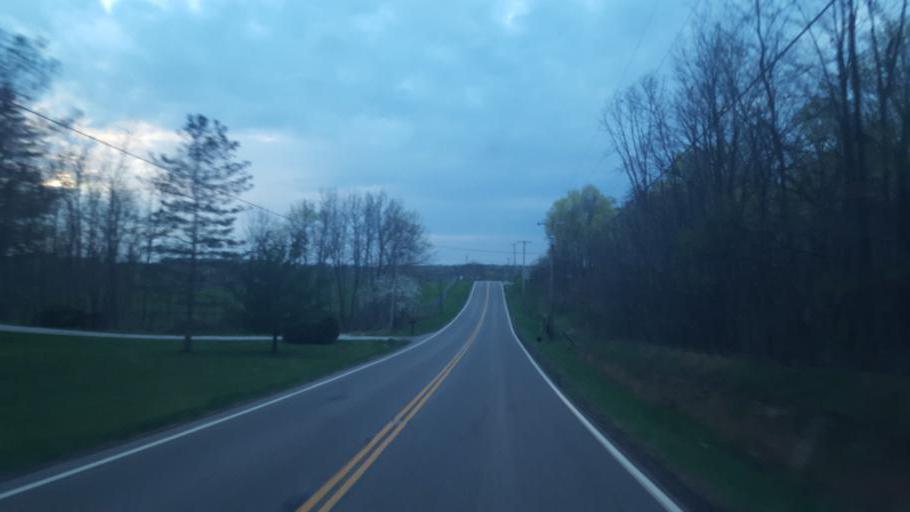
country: US
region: Ohio
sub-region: Ashland County
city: Ashland
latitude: 40.8804
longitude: -82.4185
